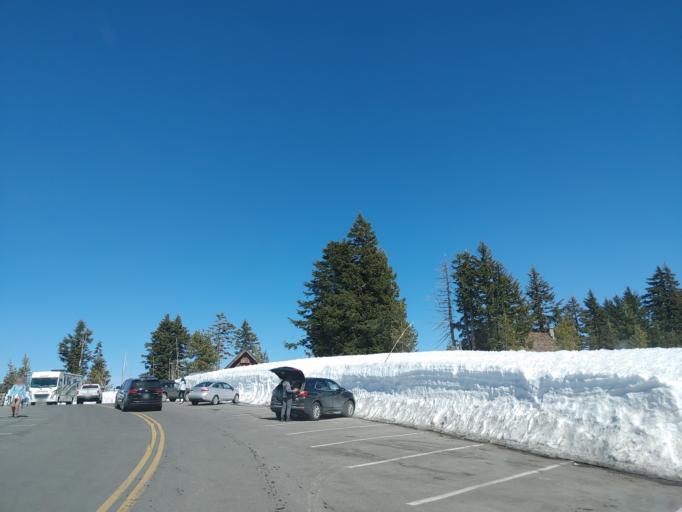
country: US
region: Oregon
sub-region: Jackson County
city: Shady Cove
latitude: 42.9109
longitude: -122.1463
